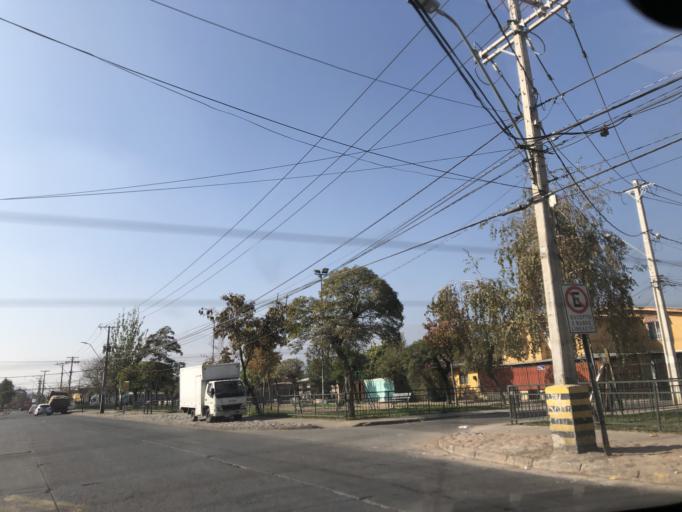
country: CL
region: Santiago Metropolitan
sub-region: Provincia de Cordillera
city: Puente Alto
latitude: -33.6149
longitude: -70.5833
